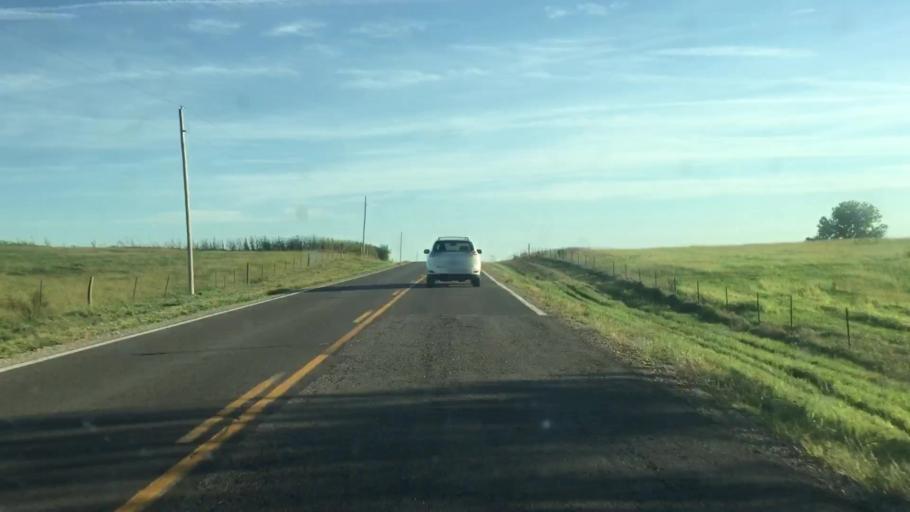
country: US
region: Kansas
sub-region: Brown County
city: Horton
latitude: 39.5835
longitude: -95.5270
